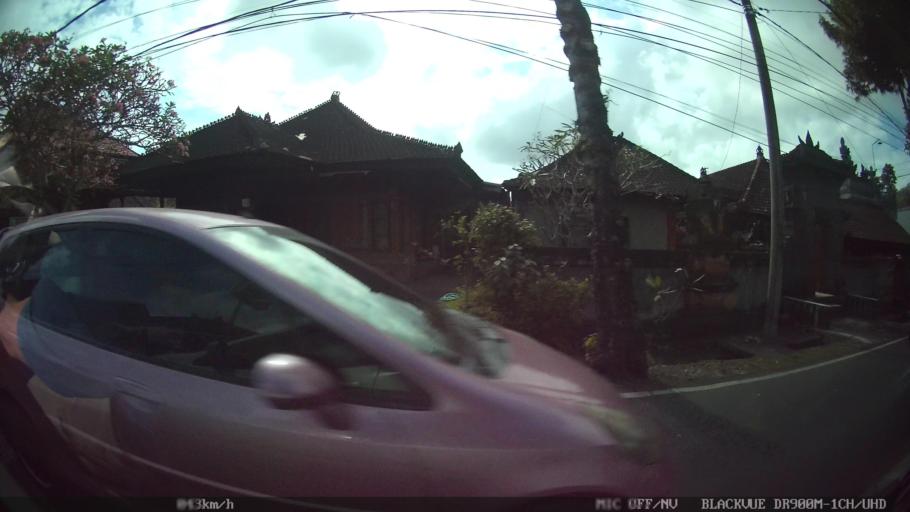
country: ID
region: Bali
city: Banjar Sedang
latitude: -8.5709
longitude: 115.2565
